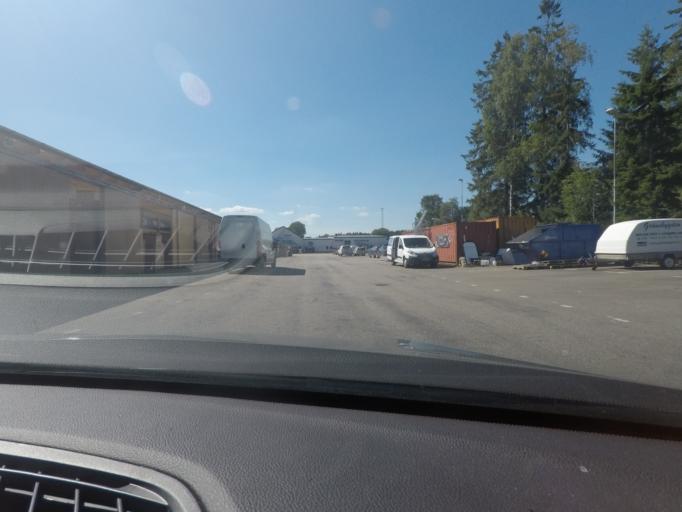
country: SE
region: Kronoberg
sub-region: Markaryds Kommun
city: Markaryd
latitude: 56.4849
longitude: 13.5315
